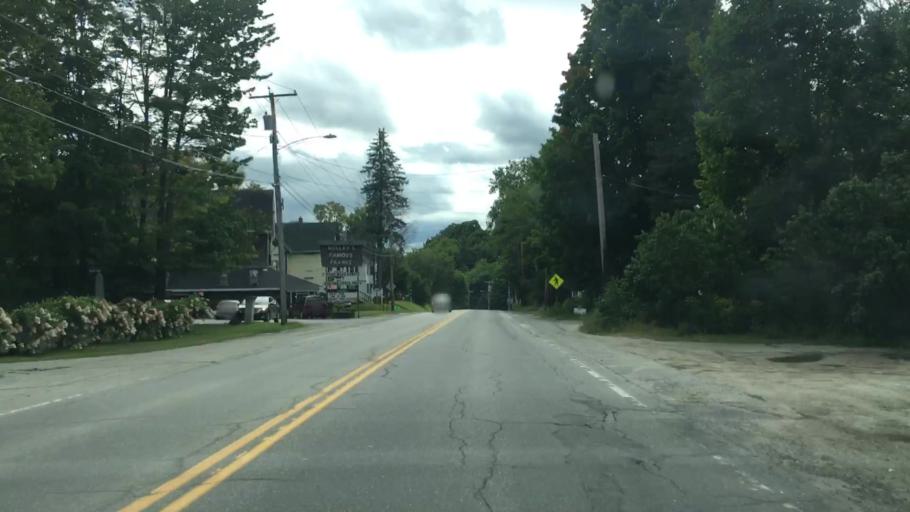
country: US
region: Maine
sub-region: Kennebec County
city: Hallowell
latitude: 44.2926
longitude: -69.7870
